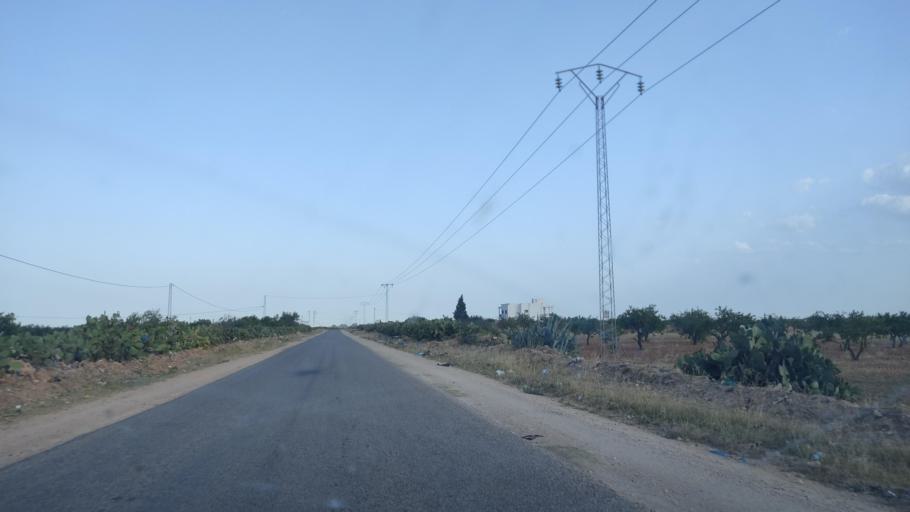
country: TN
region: Safaqis
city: Sfax
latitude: 34.8212
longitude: 10.6485
